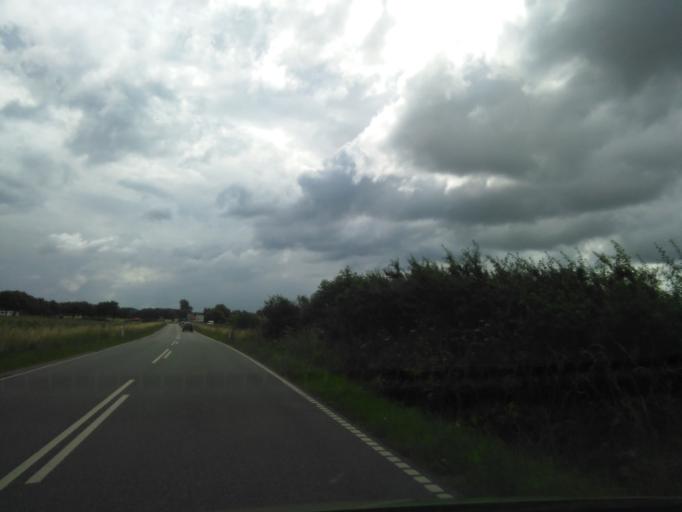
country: DK
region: Central Jutland
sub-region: Syddjurs Kommune
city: Ronde
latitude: 56.2764
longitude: 10.5030
